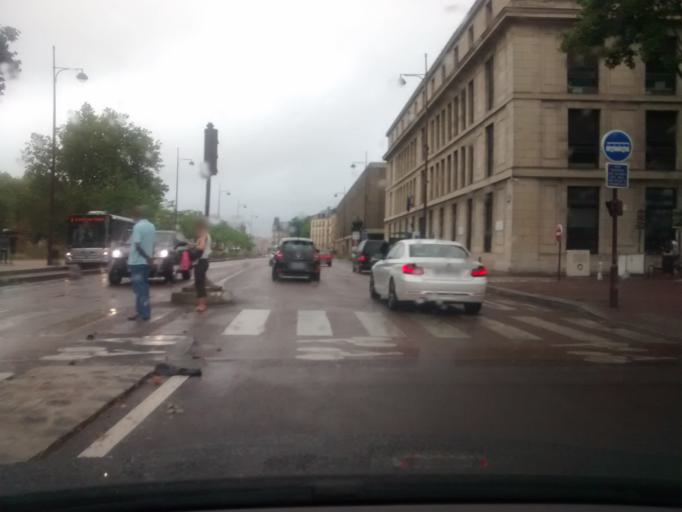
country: FR
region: Ile-de-France
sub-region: Departement des Yvelines
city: Versailles
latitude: 48.8024
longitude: 2.1299
